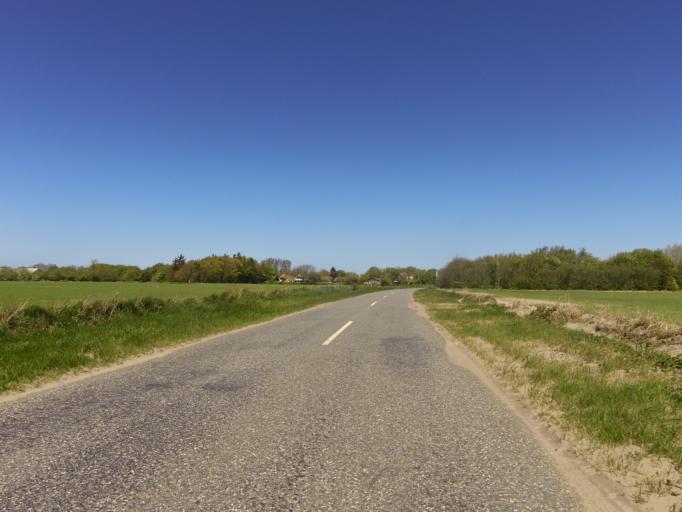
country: DK
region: South Denmark
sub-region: Tonder Kommune
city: Sherrebek
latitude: 55.2312
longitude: 8.7164
